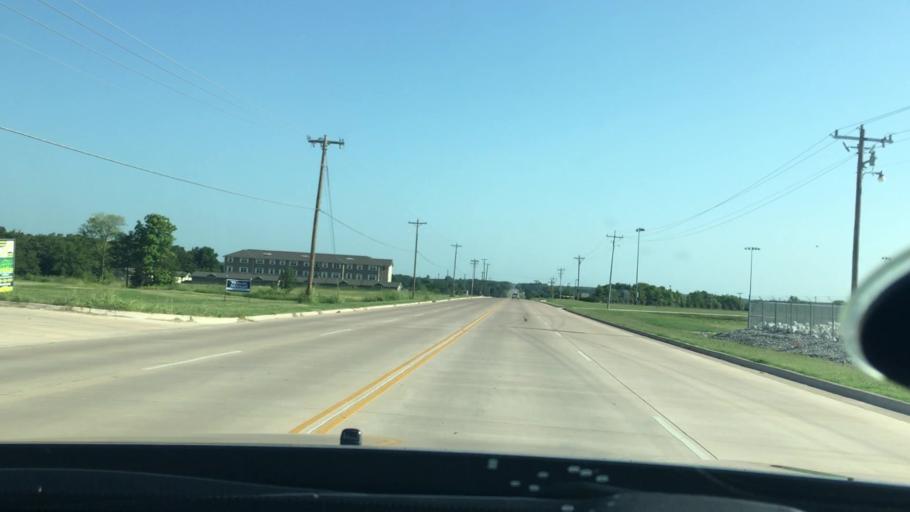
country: US
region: Oklahoma
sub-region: Pontotoc County
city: Ada
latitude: 34.7929
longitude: -96.6524
